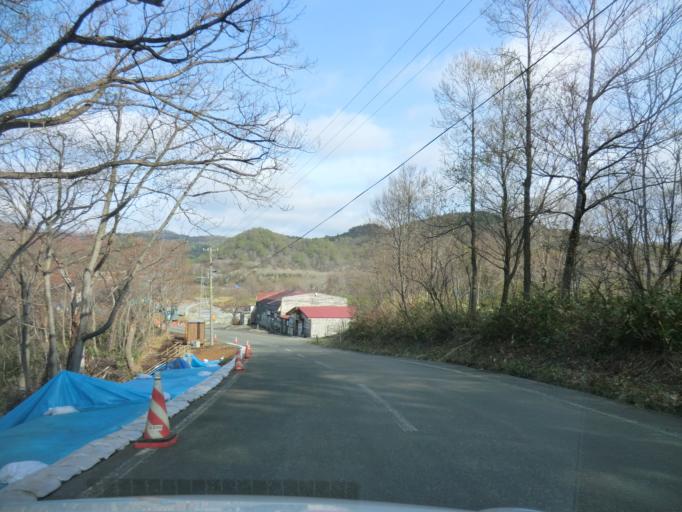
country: JP
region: Aomori
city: Mutsu
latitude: 41.3234
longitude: 141.0999
